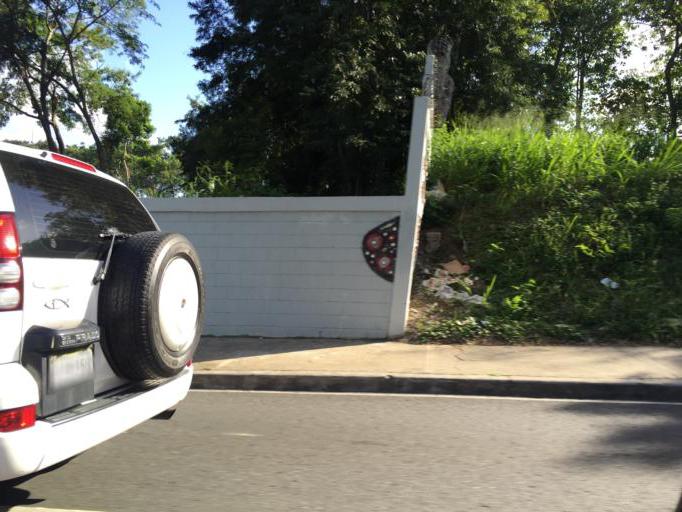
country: DO
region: Nacional
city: La Agustina
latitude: 18.4893
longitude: -69.9505
